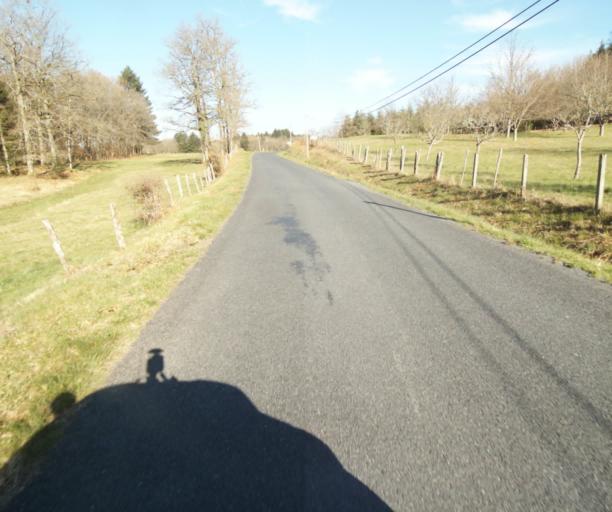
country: FR
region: Limousin
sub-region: Departement de la Correze
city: Correze
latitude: 45.2871
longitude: 1.8721
